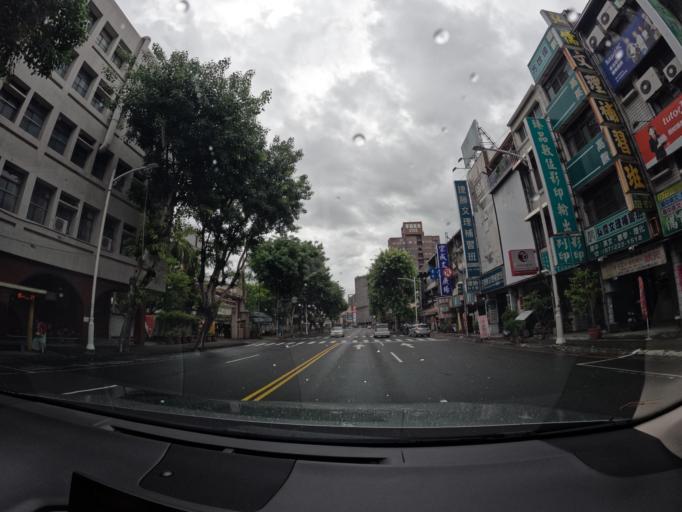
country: TW
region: Kaohsiung
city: Kaohsiung
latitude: 22.6332
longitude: 120.3223
